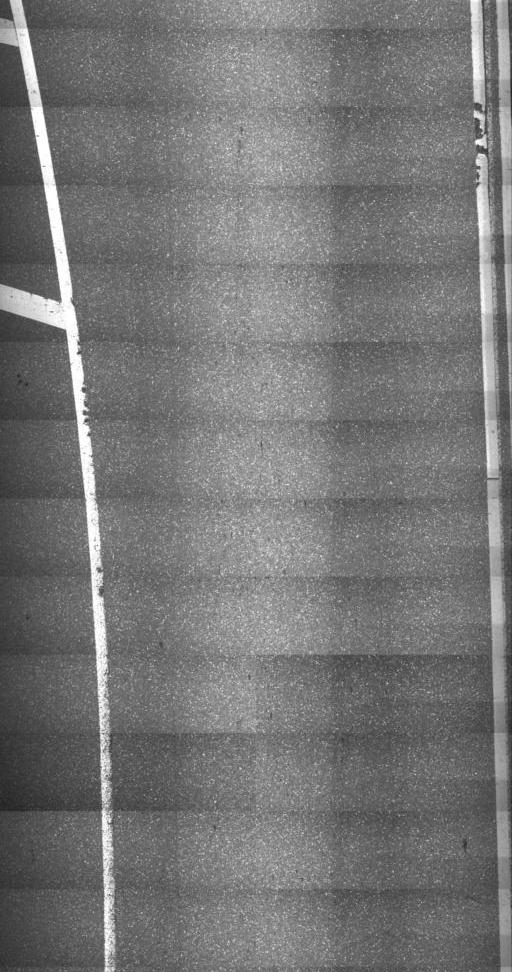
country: US
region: Vermont
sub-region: Washington County
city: Northfield
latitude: 44.1504
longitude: -72.6557
